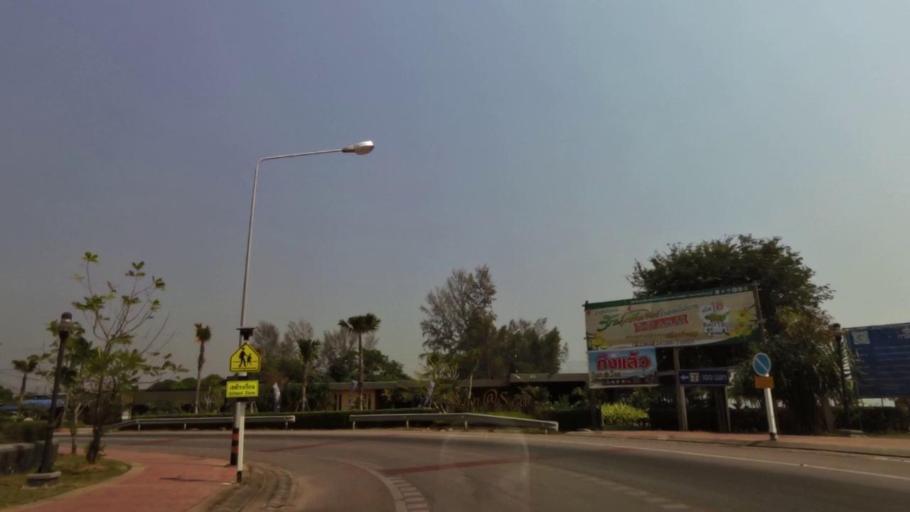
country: TH
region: Chanthaburi
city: Tha Mai
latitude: 12.5399
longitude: 101.9519
